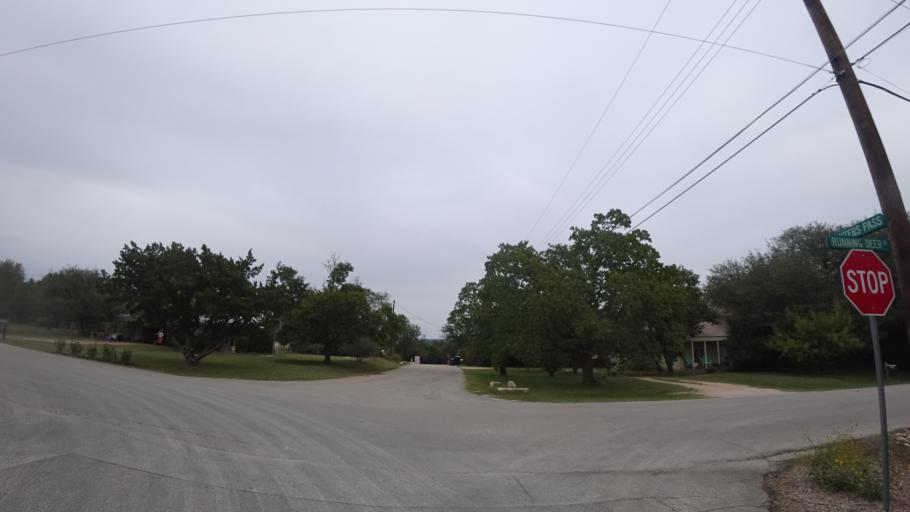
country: US
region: Texas
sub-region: Travis County
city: Hudson Bend
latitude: 30.3739
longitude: -97.9244
